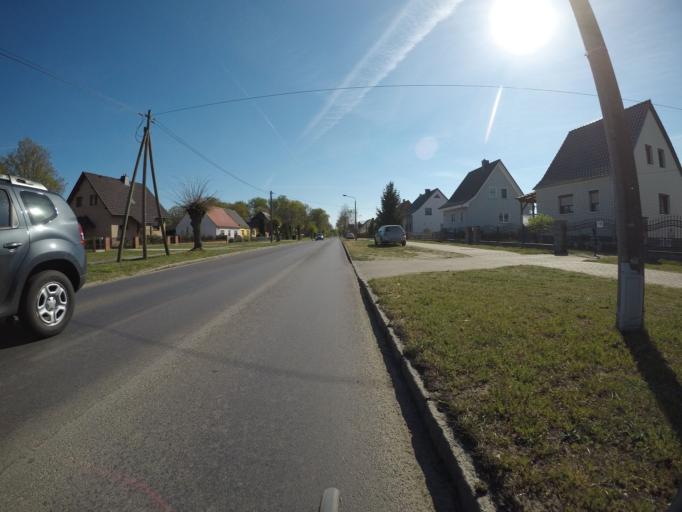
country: DE
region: Brandenburg
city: Rehfelde
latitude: 52.4992
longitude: 13.9214
